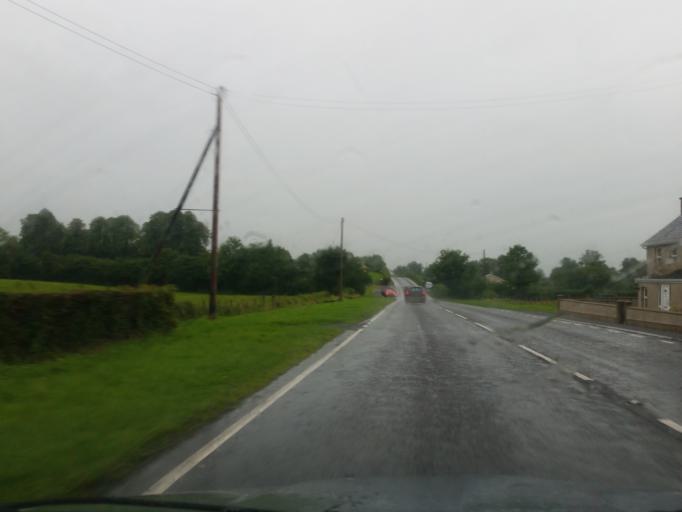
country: GB
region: Northern Ireland
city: Lisnaskea
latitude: 54.2877
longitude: -7.4654
